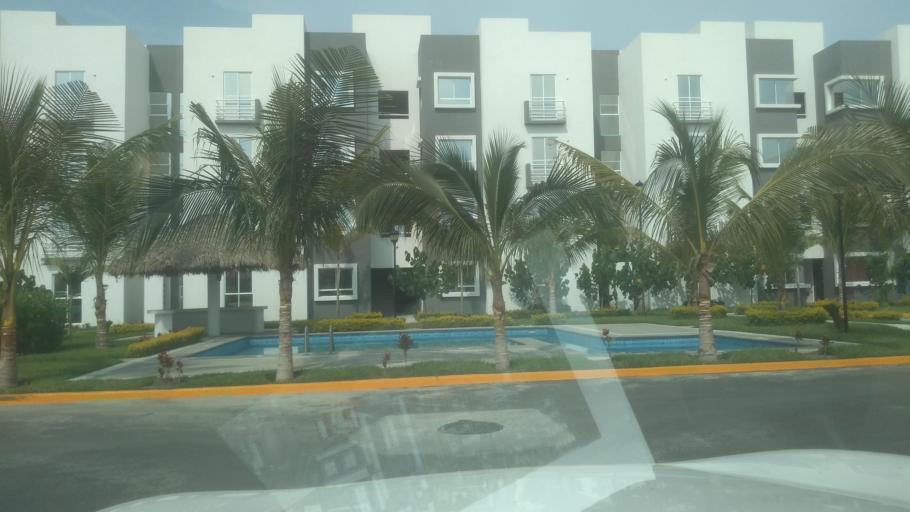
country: MX
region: Veracruz
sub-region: Veracruz
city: Lomas de Rio Medio Cuatro
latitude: 19.1773
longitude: -96.2070
